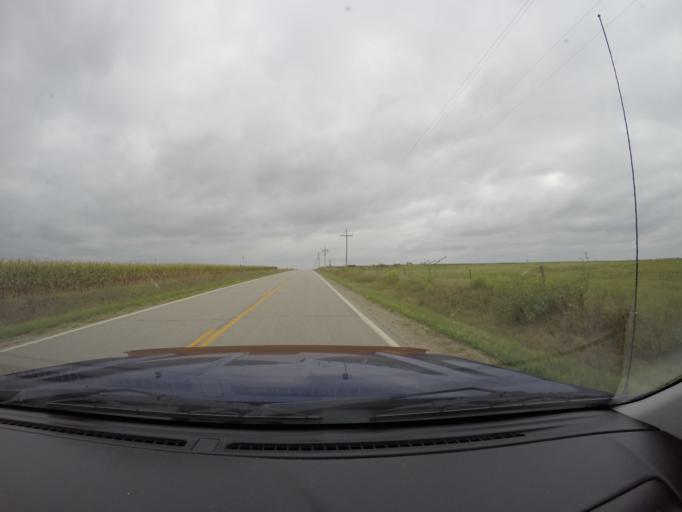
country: US
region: Kansas
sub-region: Morris County
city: Council Grove
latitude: 38.8285
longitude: -96.5941
